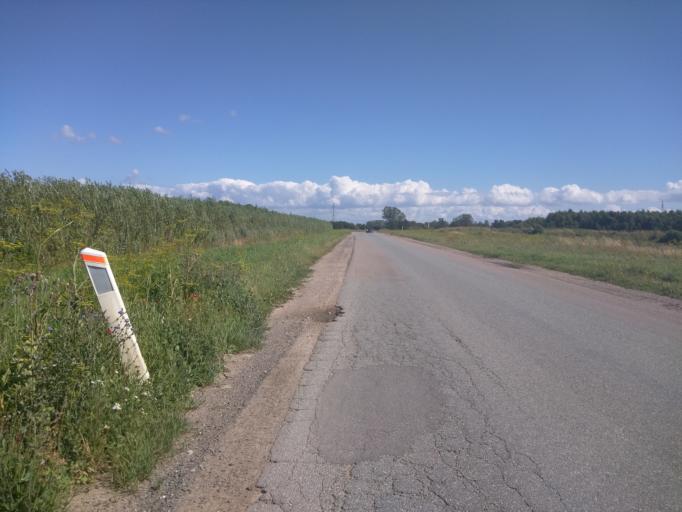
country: DK
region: Zealand
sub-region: Kalundborg Kommune
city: Svebolle
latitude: 55.6909
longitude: 11.2847
